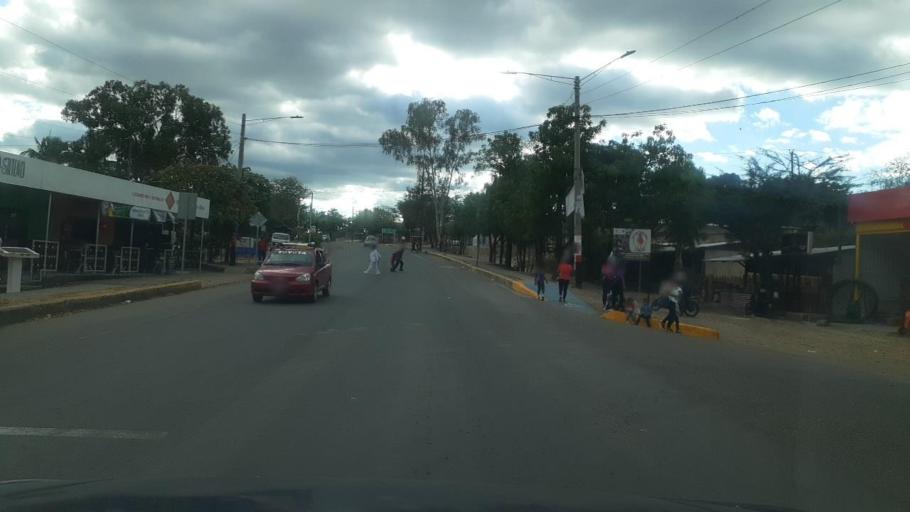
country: NI
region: Madriz
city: Somoto
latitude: 13.4882
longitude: -86.5815
